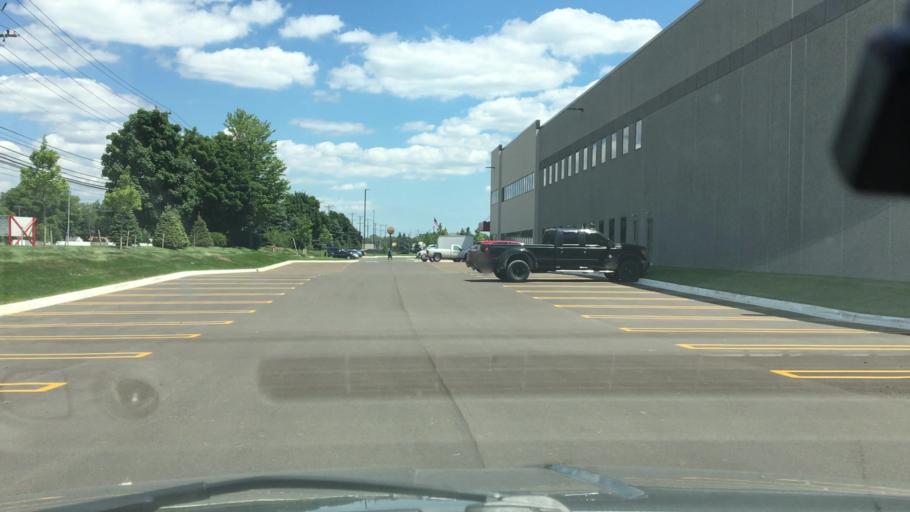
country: US
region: Michigan
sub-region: Wayne County
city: Redford
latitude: 42.3835
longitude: -83.3233
